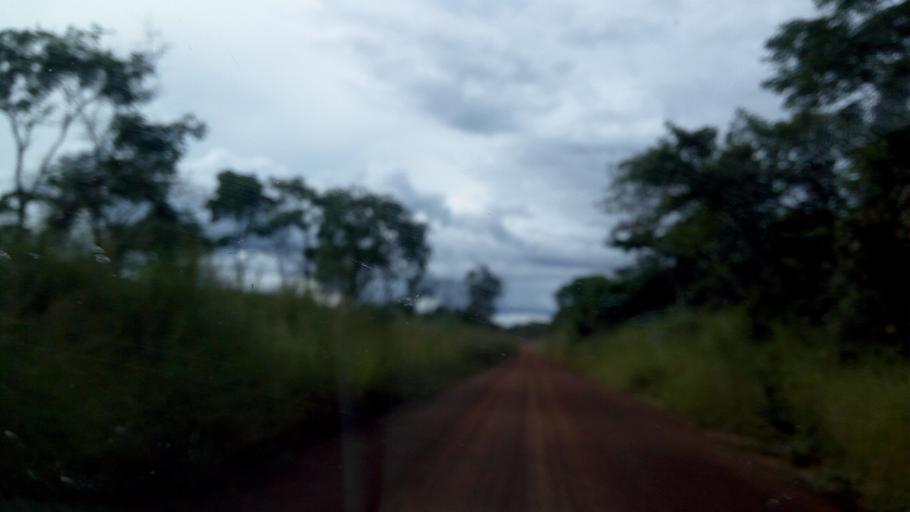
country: ZM
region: Luapula
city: Mwense
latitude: -10.3320
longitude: 28.1111
